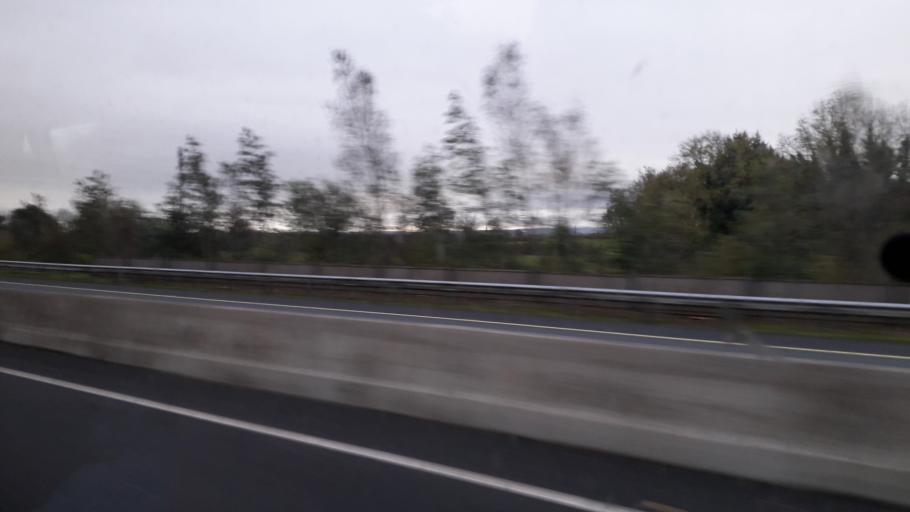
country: IE
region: Connaught
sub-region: County Galway
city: Athenry
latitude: 53.2728
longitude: -8.6839
